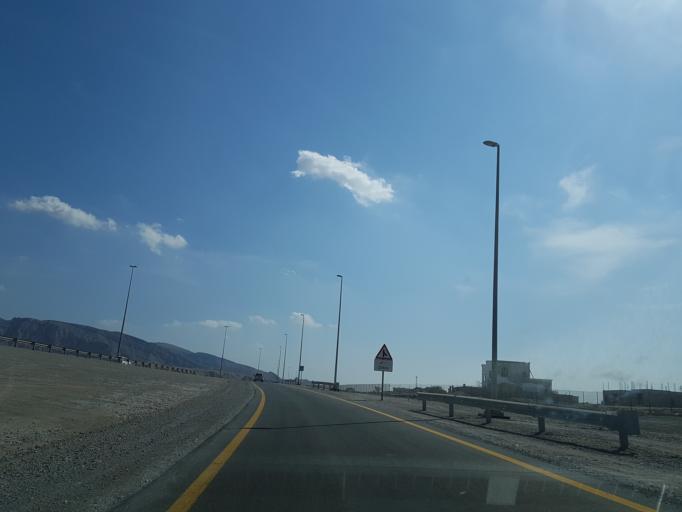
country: AE
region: Ra's al Khaymah
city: Ras al-Khaimah
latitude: 25.7967
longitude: 56.0305
